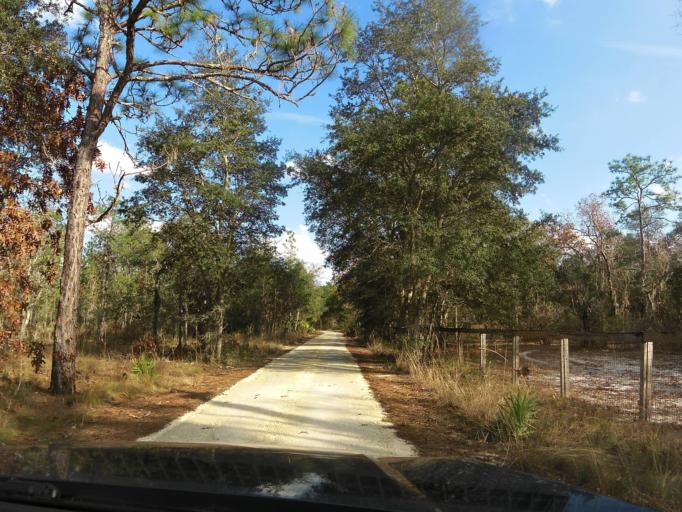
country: US
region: Florida
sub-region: Clay County
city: Middleburg
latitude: 30.1354
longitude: -81.9506
